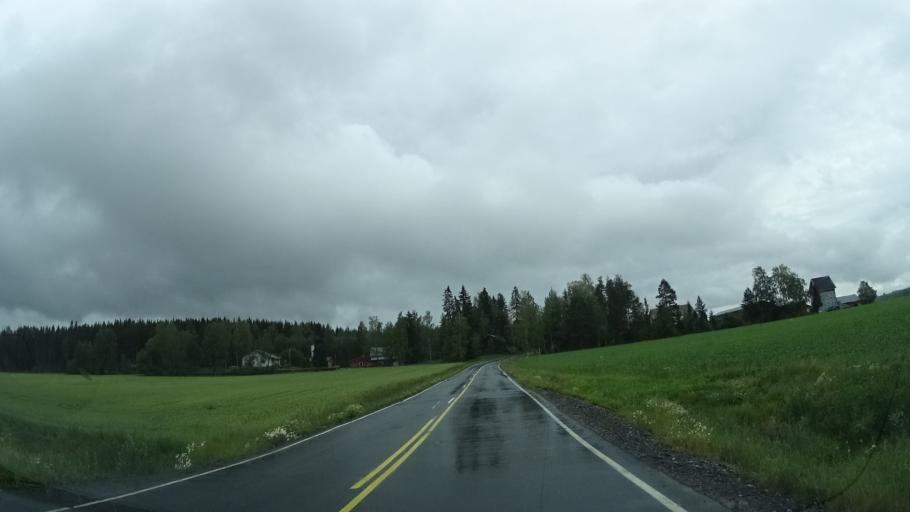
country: FI
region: Haeme
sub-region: Forssa
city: Humppila
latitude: 61.0034
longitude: 23.2518
